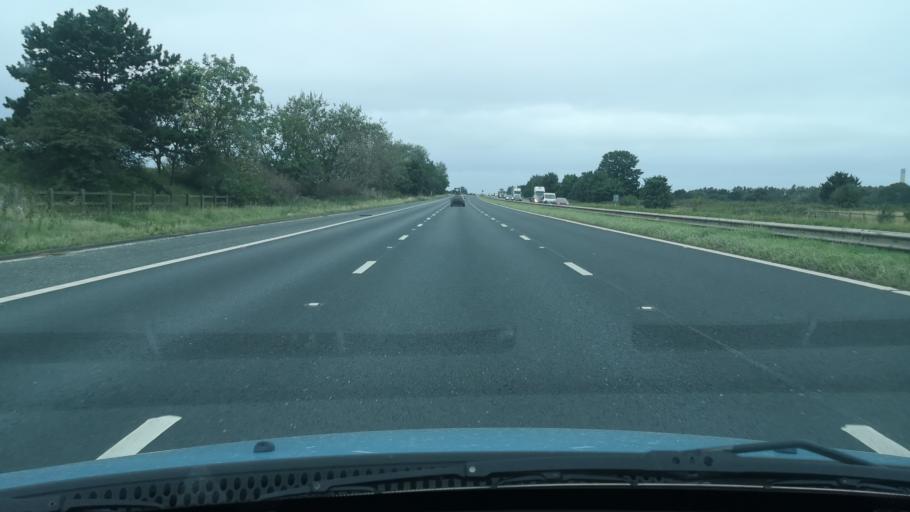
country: GB
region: England
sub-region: East Riding of Yorkshire
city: Pollington
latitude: 53.6859
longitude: -1.0900
